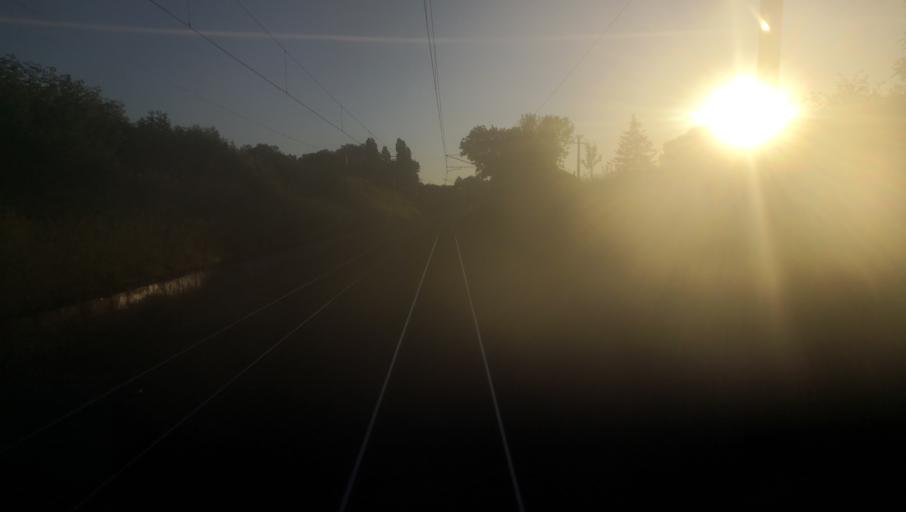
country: FR
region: Centre
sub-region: Departement du Cher
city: Cuffy
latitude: 46.9411
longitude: 3.0828
